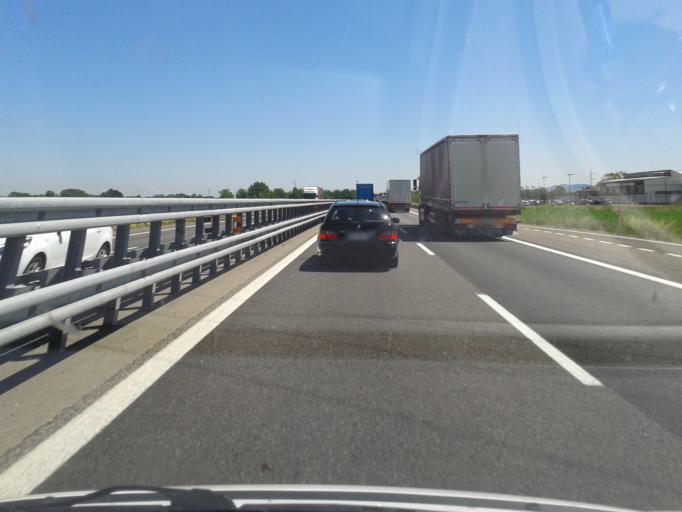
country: IT
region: Lombardy
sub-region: Provincia di Pavia
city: Voghera
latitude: 45.0140
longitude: 9.0076
